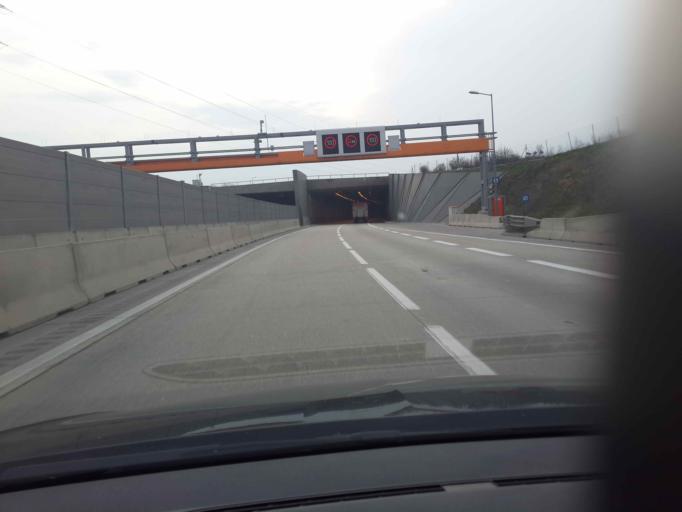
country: AT
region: Lower Austria
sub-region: Politischer Bezirk Wien-Umgebung
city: Schwechat
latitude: 48.1237
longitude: 16.4783
